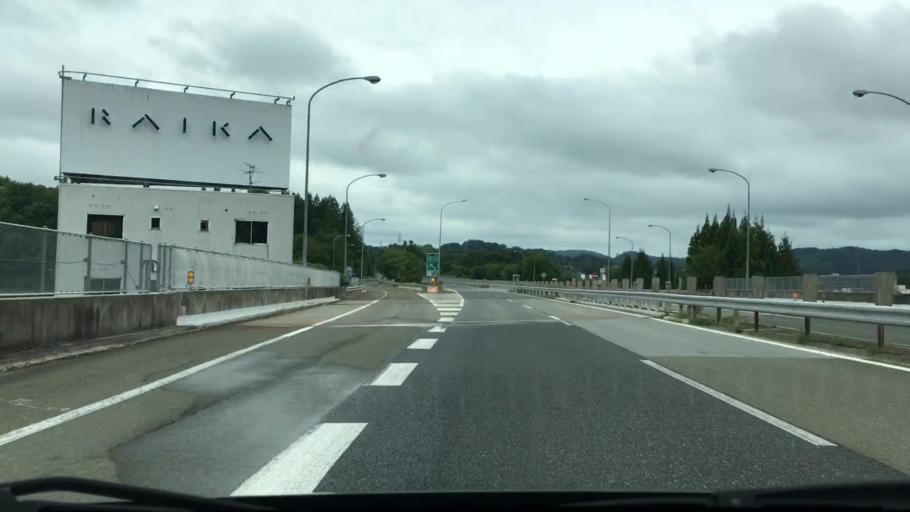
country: JP
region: Hiroshima
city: Shobara
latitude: 34.8452
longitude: 133.0266
